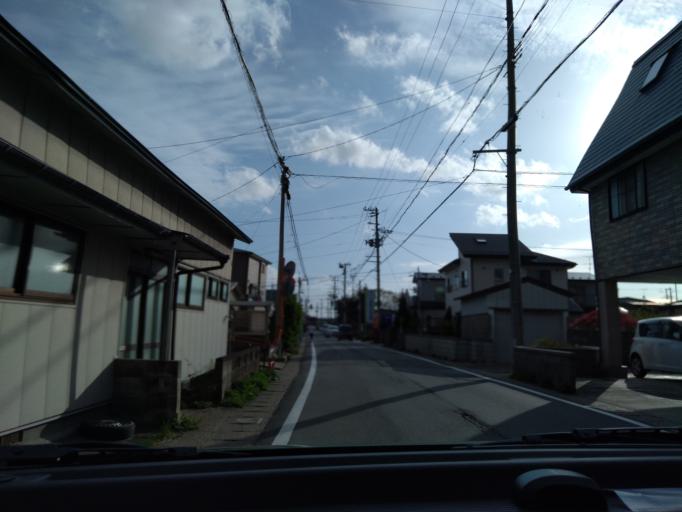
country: JP
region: Akita
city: Akita Shi
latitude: 39.7676
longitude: 140.0800
